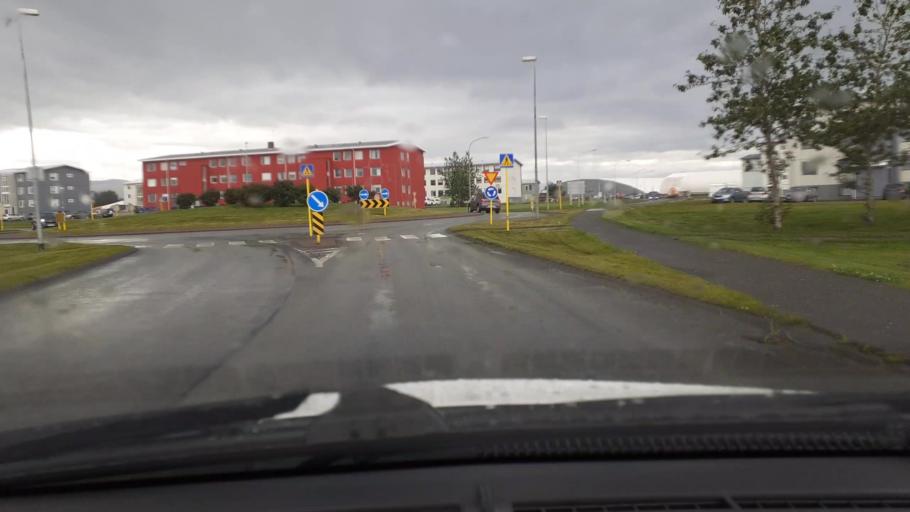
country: IS
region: West
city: Akranes
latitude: 64.3215
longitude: -22.0602
